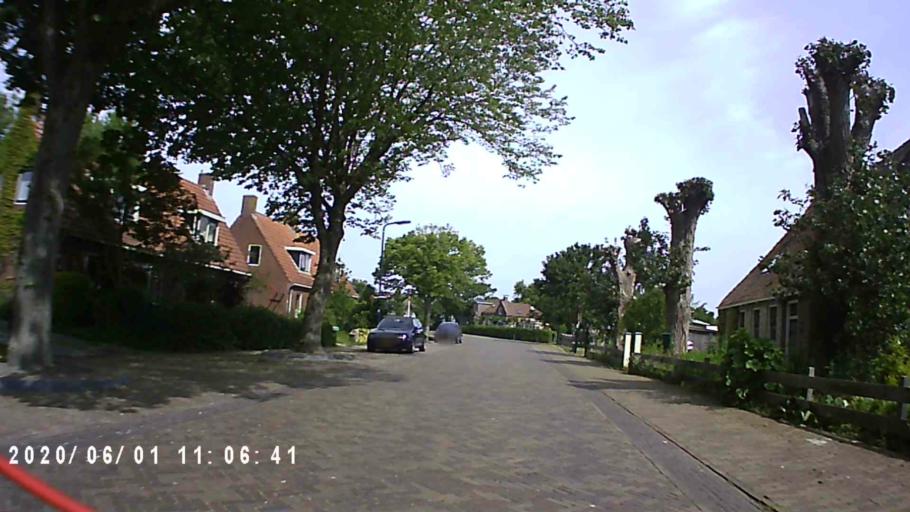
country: NL
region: Friesland
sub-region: Gemeente Franekeradeel
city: Sexbierum
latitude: 53.1958
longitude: 5.4607
